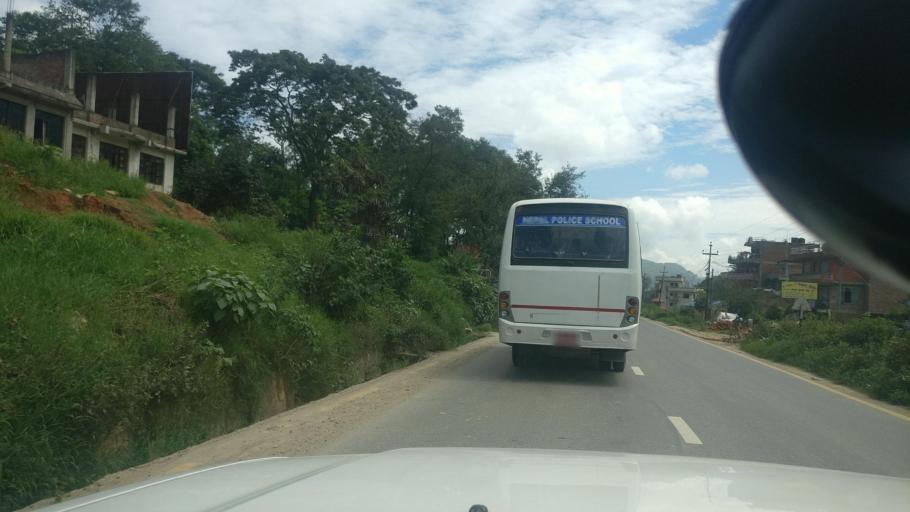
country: NP
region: Central Region
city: Banepa
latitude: 27.6316
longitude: 85.4960
